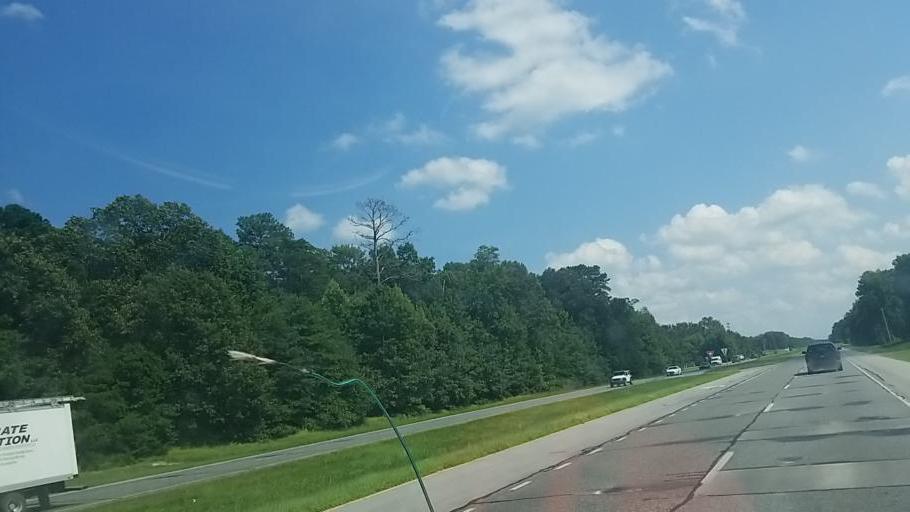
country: US
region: Delaware
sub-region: Sussex County
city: Georgetown
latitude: 38.7550
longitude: -75.4370
